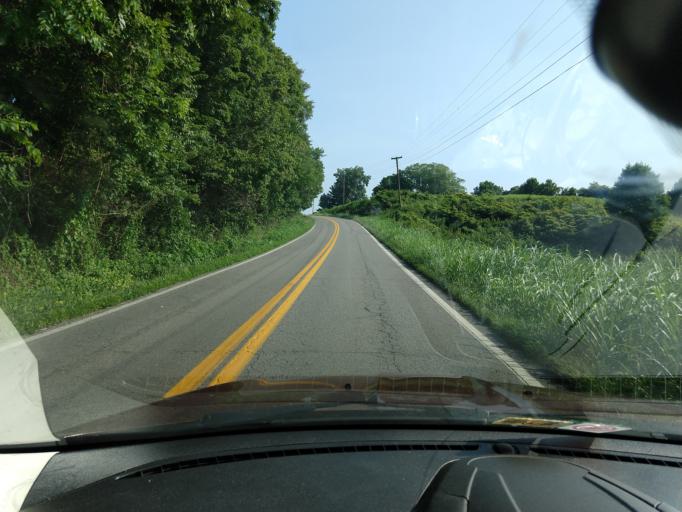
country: US
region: West Virginia
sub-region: Mason County
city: New Haven
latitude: 38.9400
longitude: -81.9188
